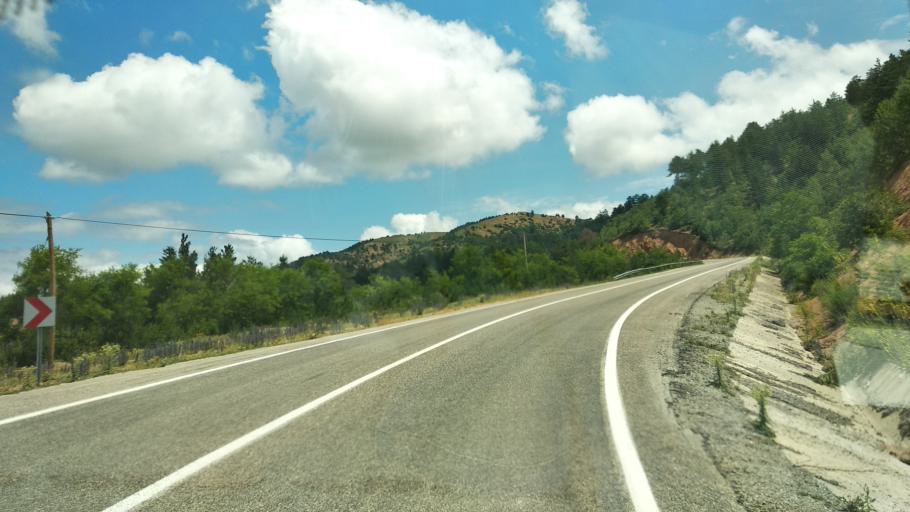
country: TR
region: Gumushane
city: Kose
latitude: 40.2983
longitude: 39.5592
